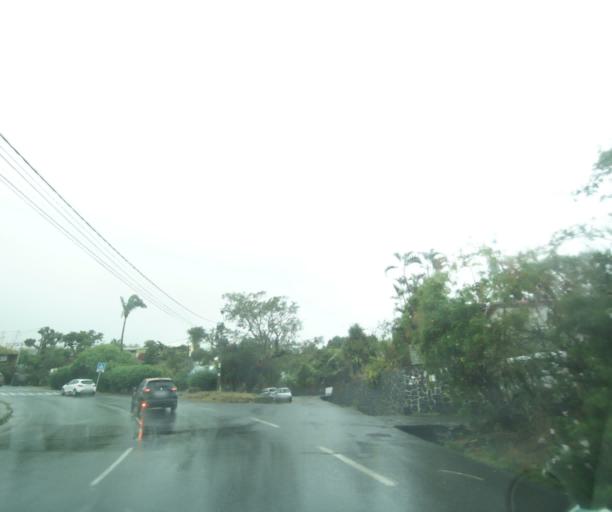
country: RE
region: Reunion
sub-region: Reunion
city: Saint-Paul
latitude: -21.0352
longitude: 55.2720
